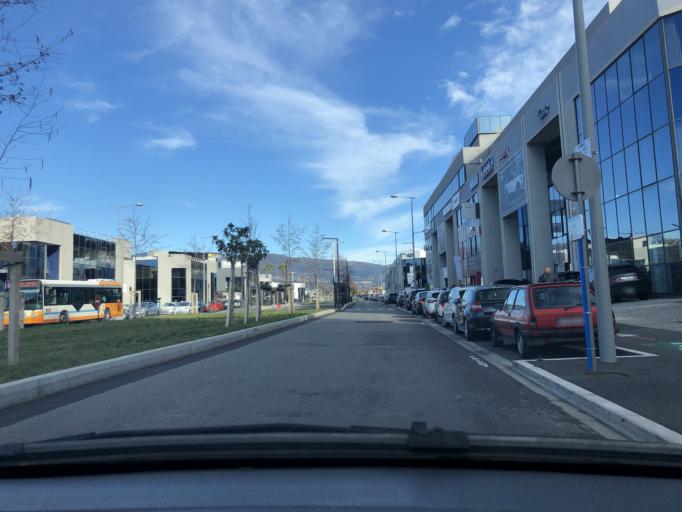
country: FR
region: Provence-Alpes-Cote d'Azur
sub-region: Departement des Alpes-Maritimes
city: Saint-Laurent-du-Var
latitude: 43.6867
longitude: 7.2019
